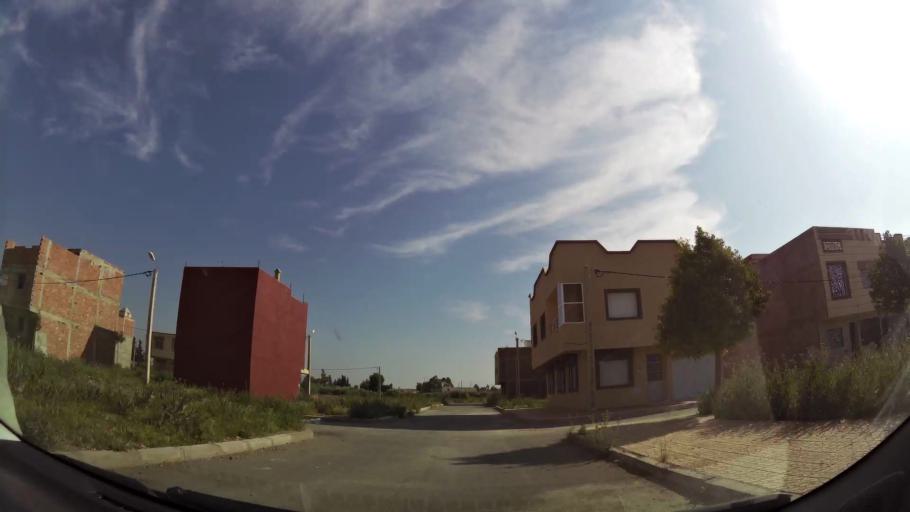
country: MA
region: Oriental
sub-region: Oujda-Angad
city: Oujda
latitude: 34.7246
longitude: -1.8805
